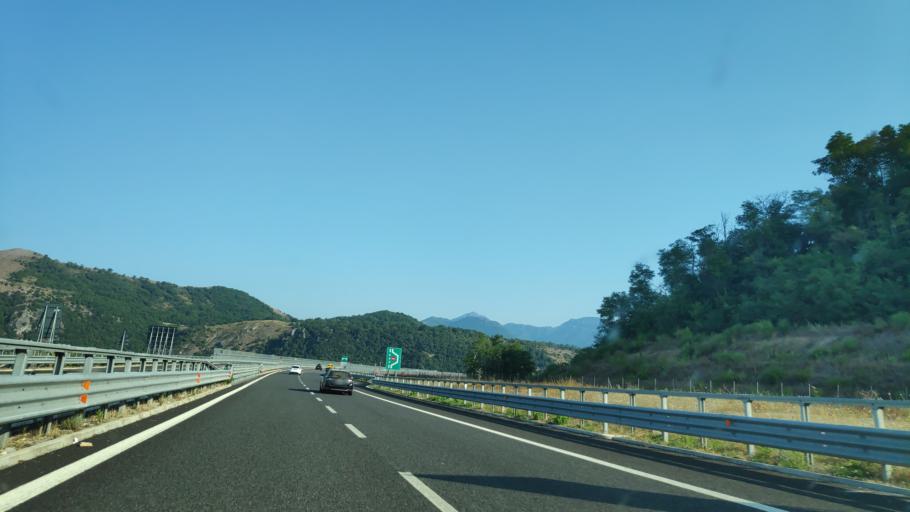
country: IT
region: Calabria
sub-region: Provincia di Cosenza
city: Laino Castello-Nuovo Centro
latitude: 39.9325
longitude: 15.9625
